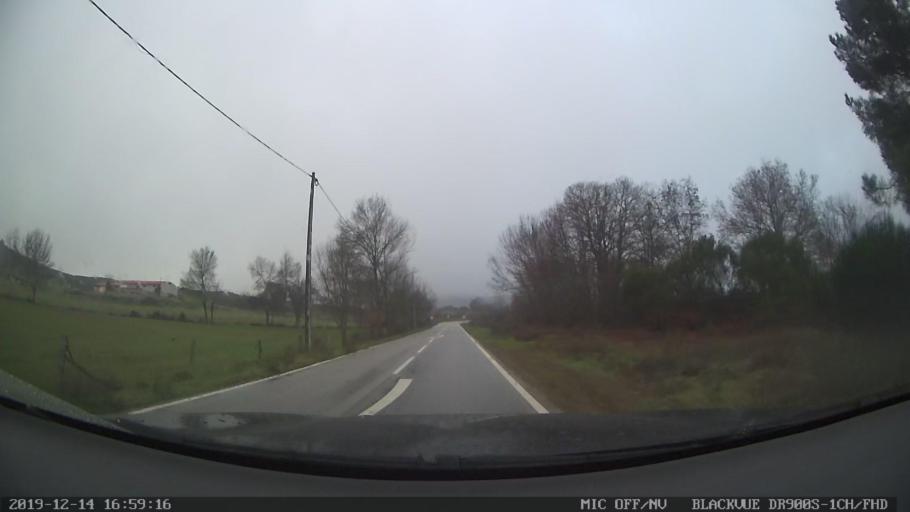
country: PT
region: Vila Real
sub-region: Vila Pouca de Aguiar
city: Vila Pouca de Aguiar
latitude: 41.4352
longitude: -7.5608
